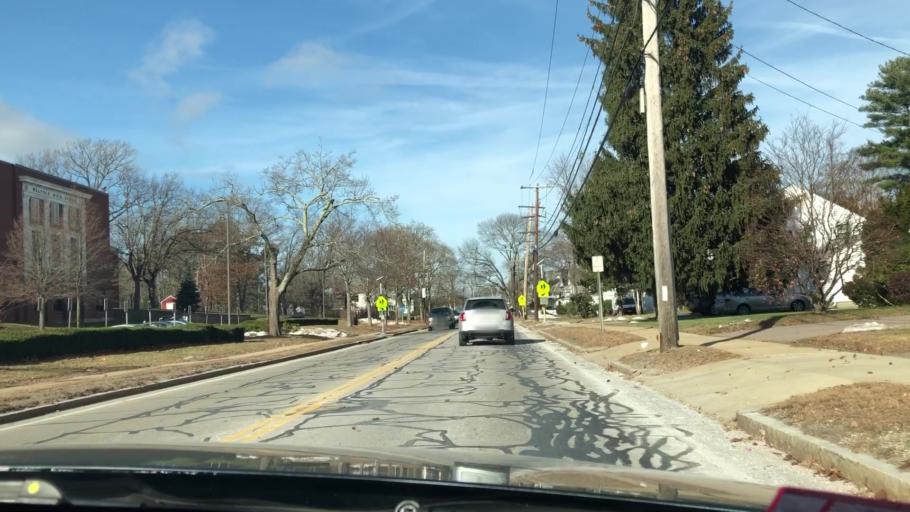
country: US
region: Massachusetts
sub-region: Norfolk County
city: Walpole
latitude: 42.1364
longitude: -71.2466
